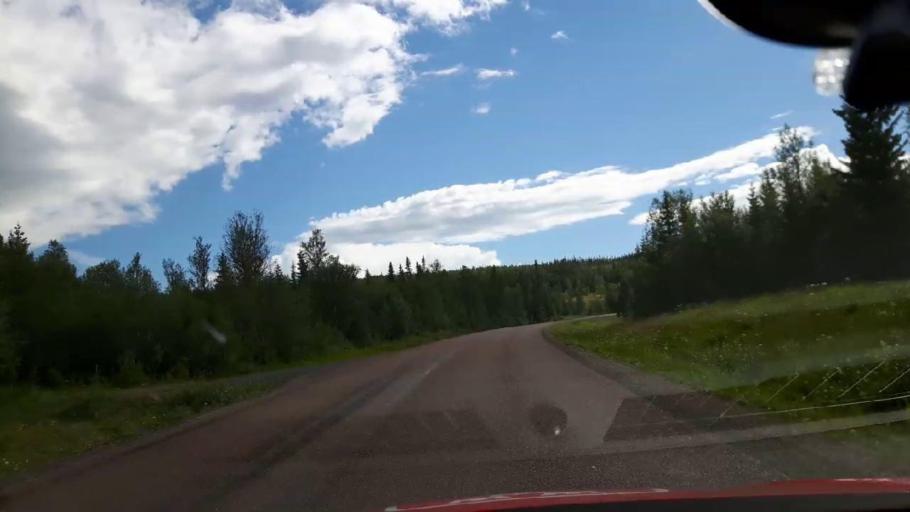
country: SE
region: Jaemtland
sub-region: Are Kommun
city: Are
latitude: 63.2826
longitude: 13.2375
